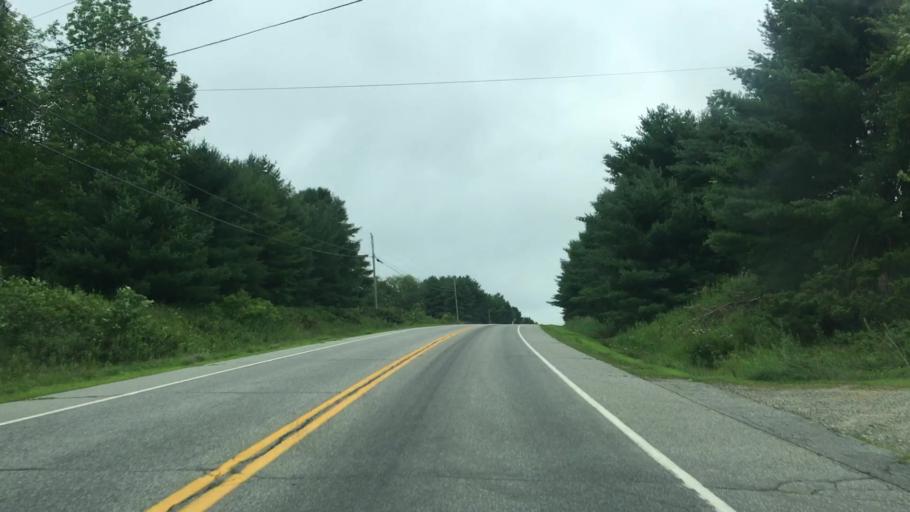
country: US
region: Maine
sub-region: Sagadahoc County
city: Richmond
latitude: 44.1125
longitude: -69.7311
